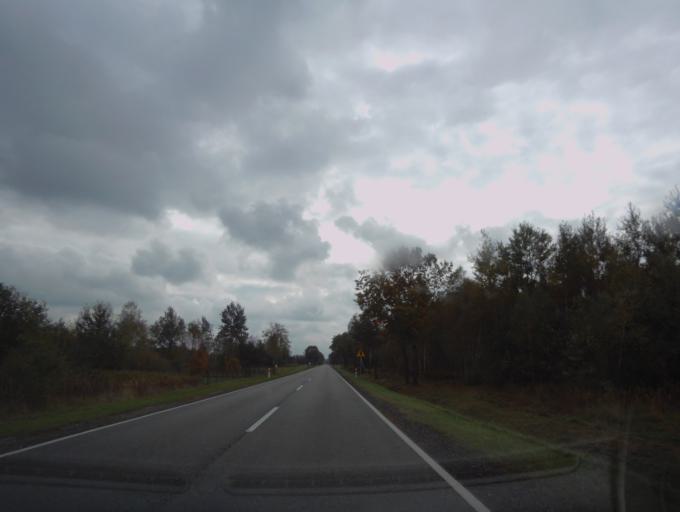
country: PL
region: Subcarpathian Voivodeship
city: Nowa Sarzyna
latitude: 50.3458
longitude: 22.3259
